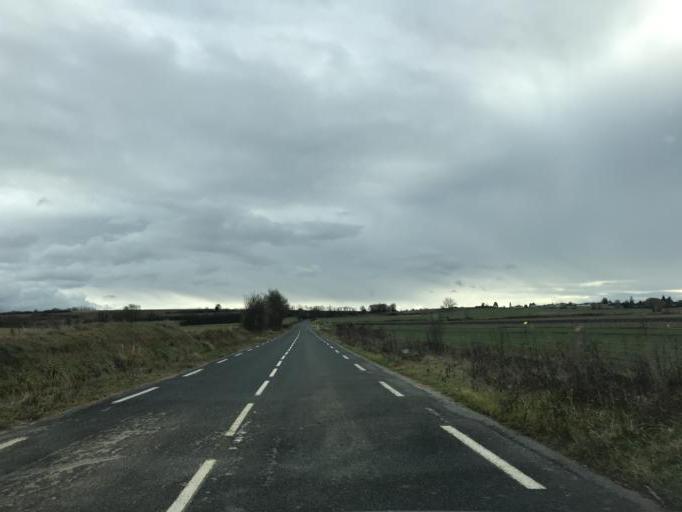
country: FR
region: Rhone-Alpes
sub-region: Departement de l'Ain
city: Miribel
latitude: 45.8444
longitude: 4.9374
